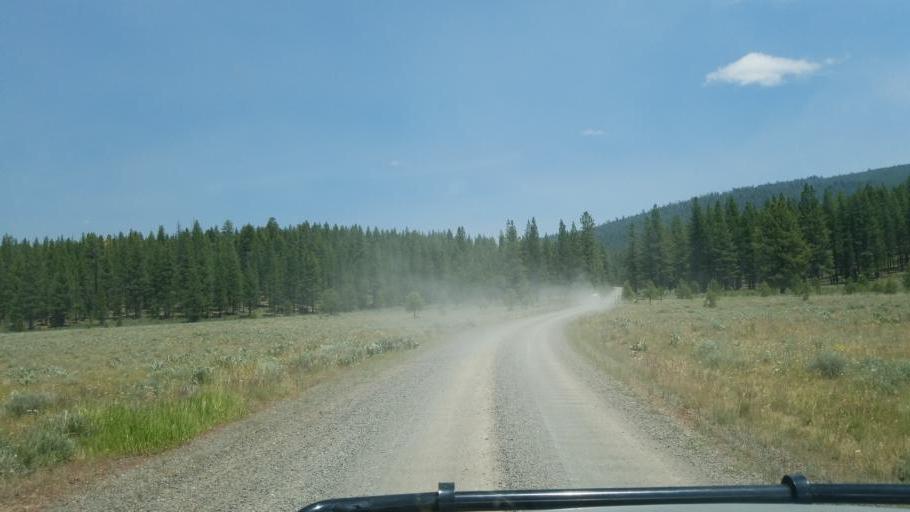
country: US
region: California
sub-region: Lassen County
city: Westwood
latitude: 40.5979
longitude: -120.9560
